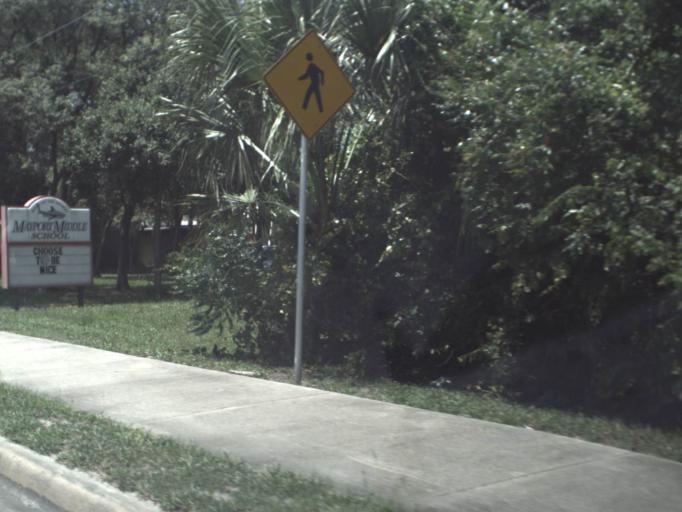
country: US
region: Florida
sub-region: Duval County
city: Atlantic Beach
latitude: 30.3633
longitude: -81.4121
